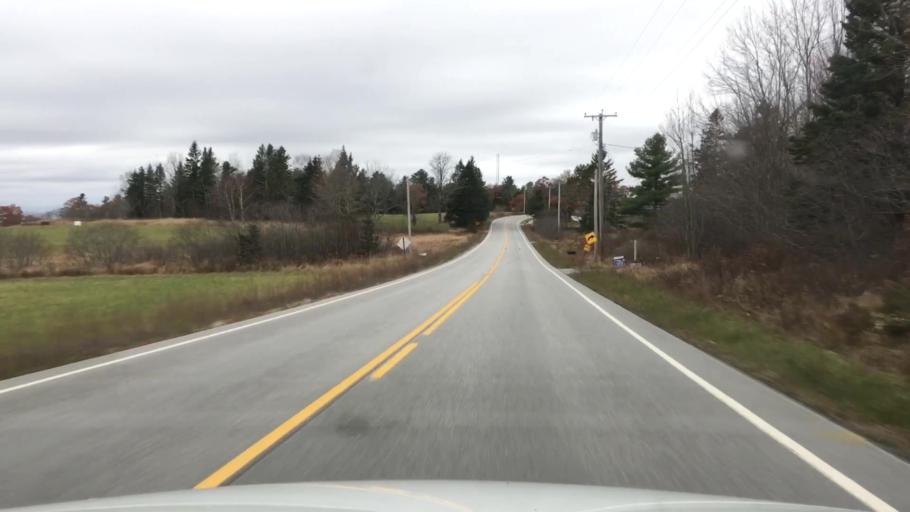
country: US
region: Maine
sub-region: Hancock County
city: Penobscot
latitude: 44.5295
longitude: -68.6718
